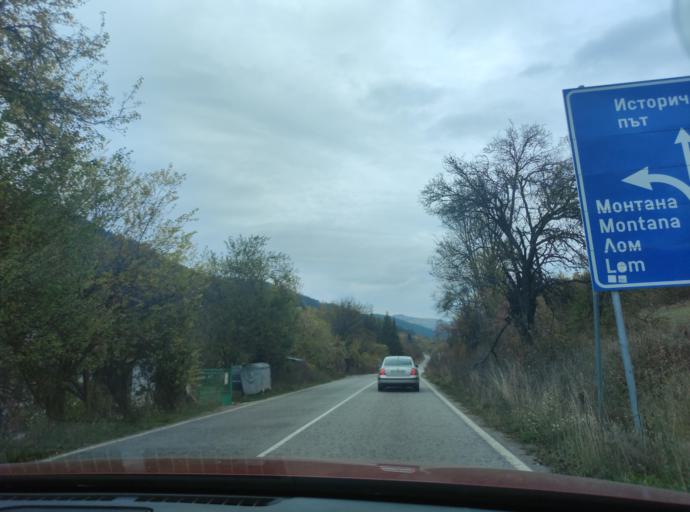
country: BG
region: Sofiya
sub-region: Obshtina Godech
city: Godech
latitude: 43.0372
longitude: 23.1371
